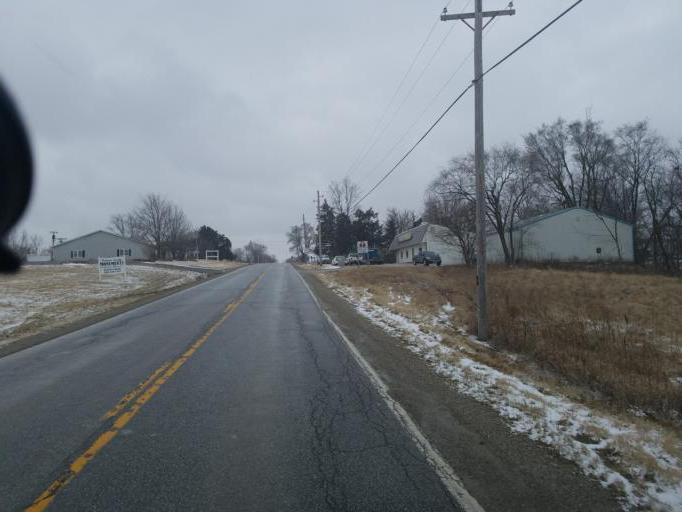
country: US
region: Missouri
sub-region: Putnam County
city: Unionville
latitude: 40.4844
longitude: -93.0092
